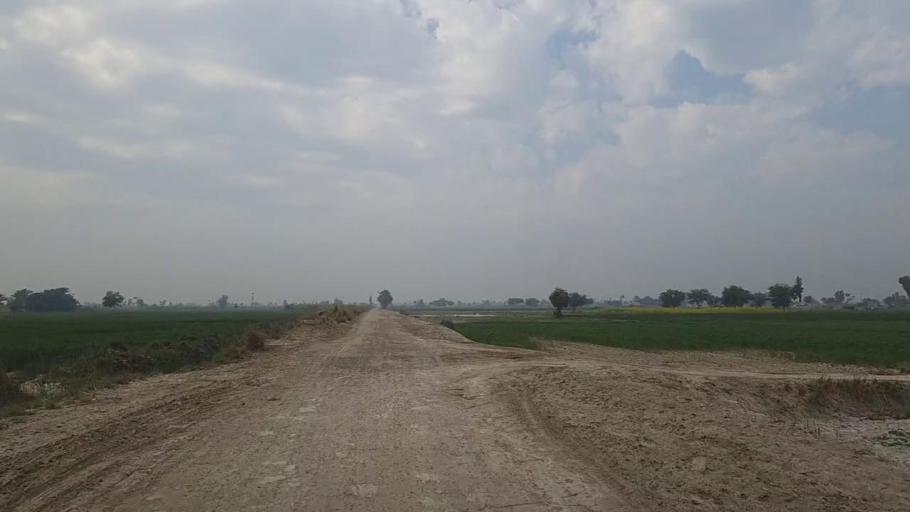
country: PK
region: Sindh
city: Nawabshah
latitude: 26.3608
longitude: 68.3911
